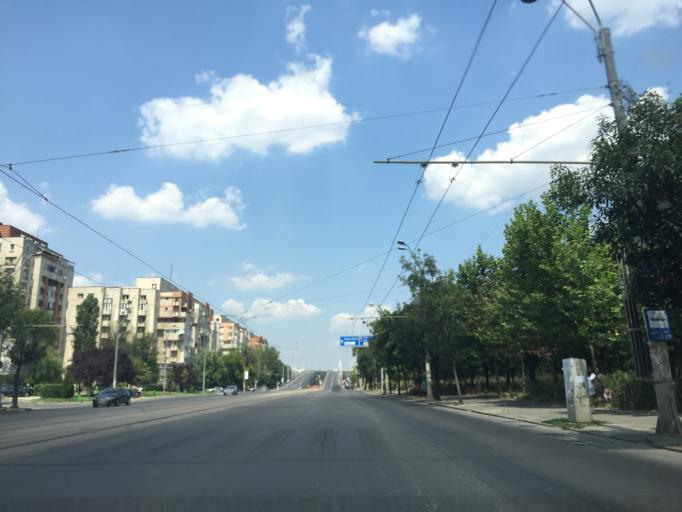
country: RO
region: Bucuresti
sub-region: Municipiul Bucuresti
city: Bucharest
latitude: 44.4035
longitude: 26.1212
